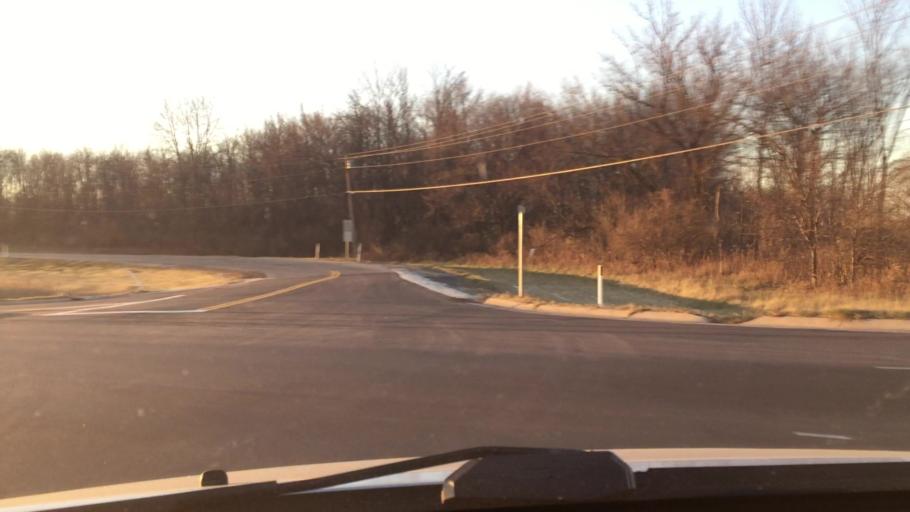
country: US
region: Wisconsin
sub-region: Waukesha County
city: Lannon
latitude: 43.0867
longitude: -88.1682
